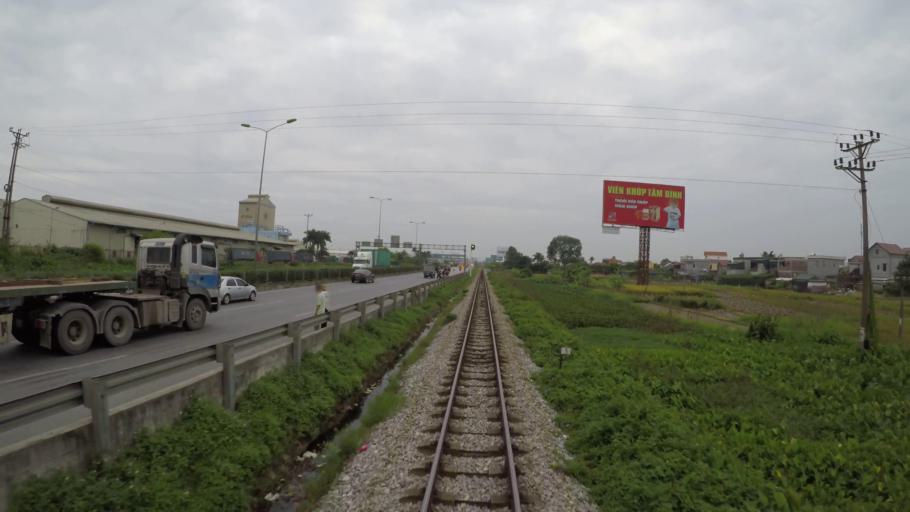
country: VN
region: Hai Duong
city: Nam Sach
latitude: 20.9671
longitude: 106.3782
